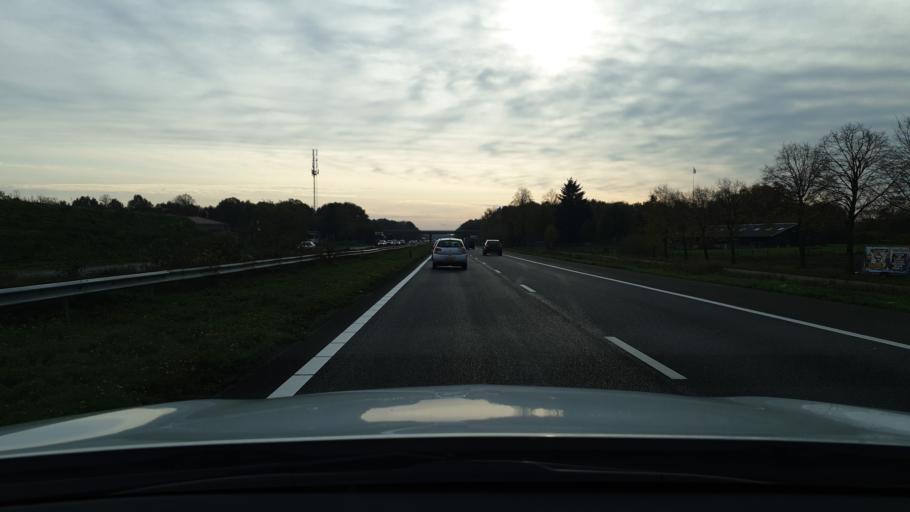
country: NL
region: North Brabant
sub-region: Gemeente Landerd
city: Schaijk
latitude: 51.7734
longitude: 5.6322
